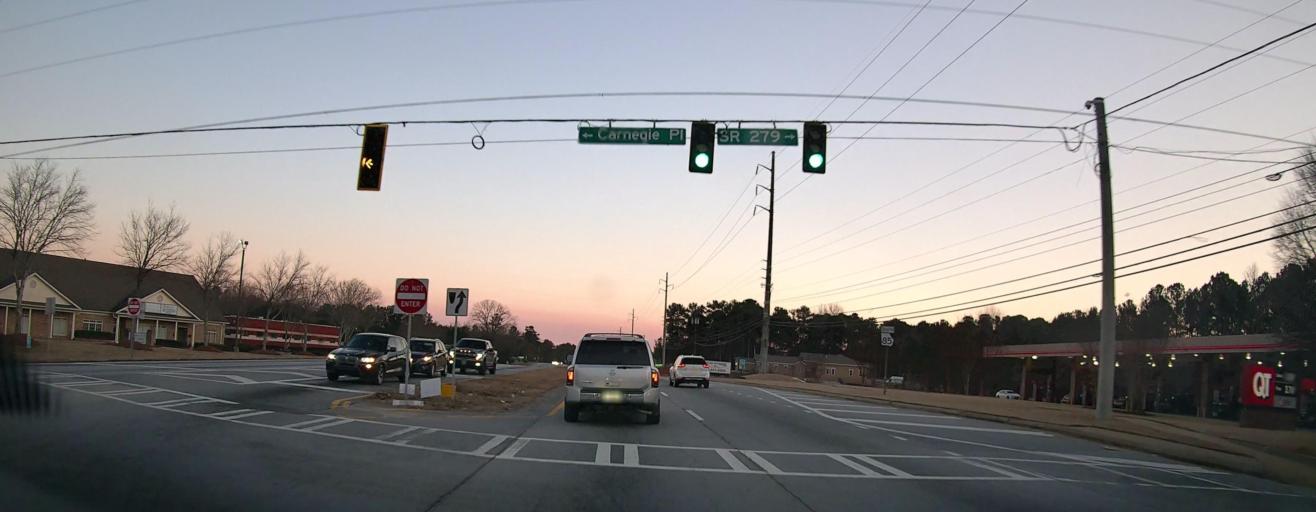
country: US
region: Georgia
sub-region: Clayton County
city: Riverdale
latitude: 33.5095
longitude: -84.4298
